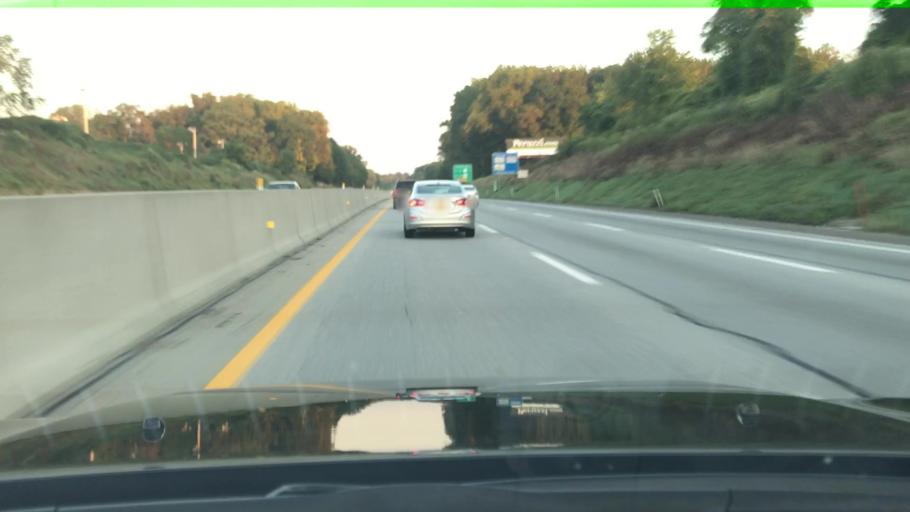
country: US
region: Pennsylvania
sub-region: Bucks County
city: Feasterville
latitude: 40.1509
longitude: -75.0232
